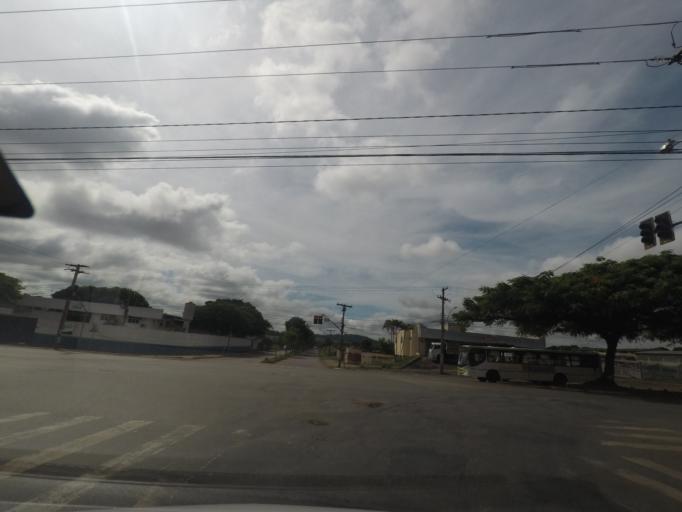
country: BR
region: Goias
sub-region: Goiania
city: Goiania
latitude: -16.6600
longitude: -49.2107
